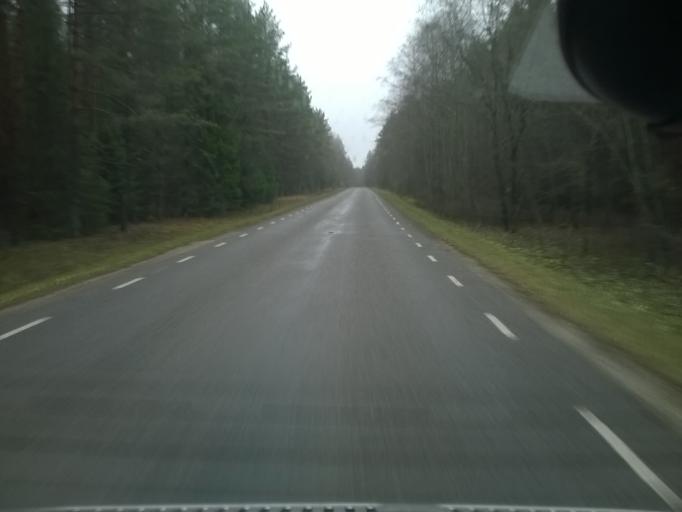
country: EE
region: Raplamaa
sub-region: Kohila vald
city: Kohila
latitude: 59.1954
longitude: 24.6641
